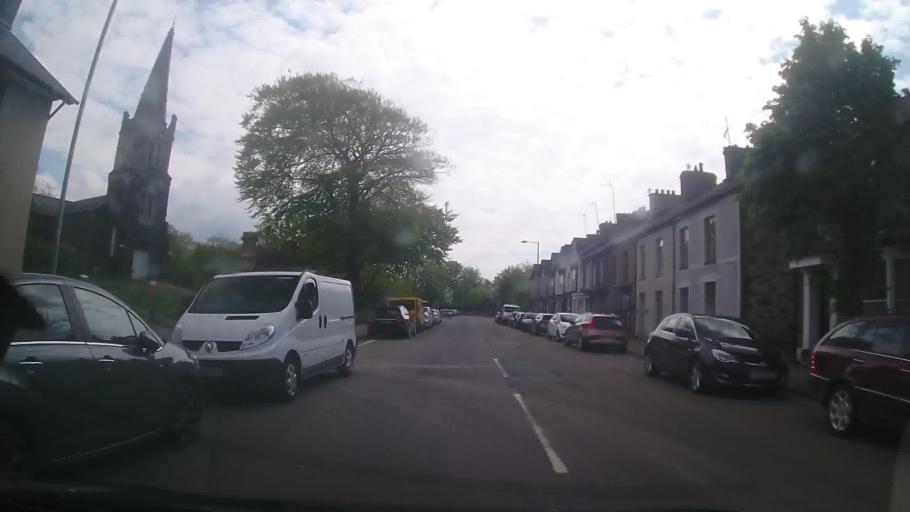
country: GB
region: Wales
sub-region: Gwynedd
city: Porthmadog
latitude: 52.9397
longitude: -4.1406
